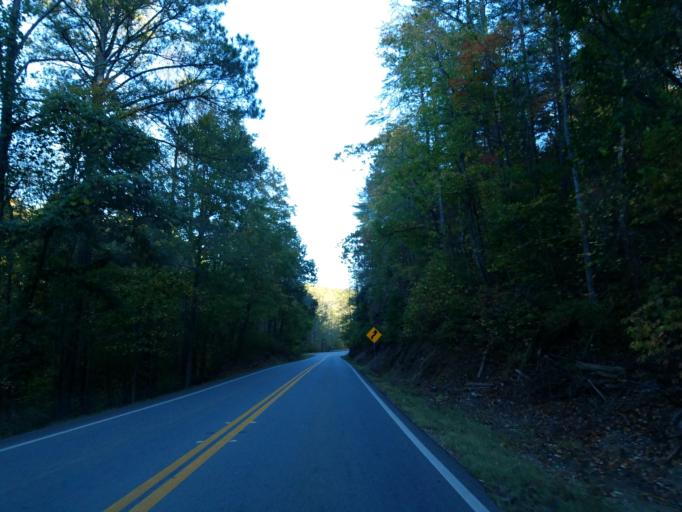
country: US
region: Georgia
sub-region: Dawson County
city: Dawsonville
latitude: 34.4275
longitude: -84.2158
